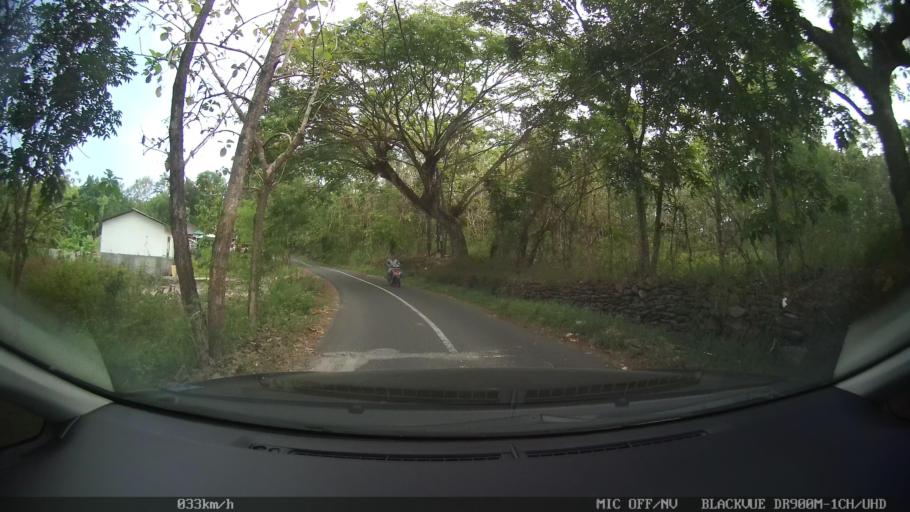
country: ID
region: Daerah Istimewa Yogyakarta
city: Bantul
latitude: -7.8596
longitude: 110.3085
